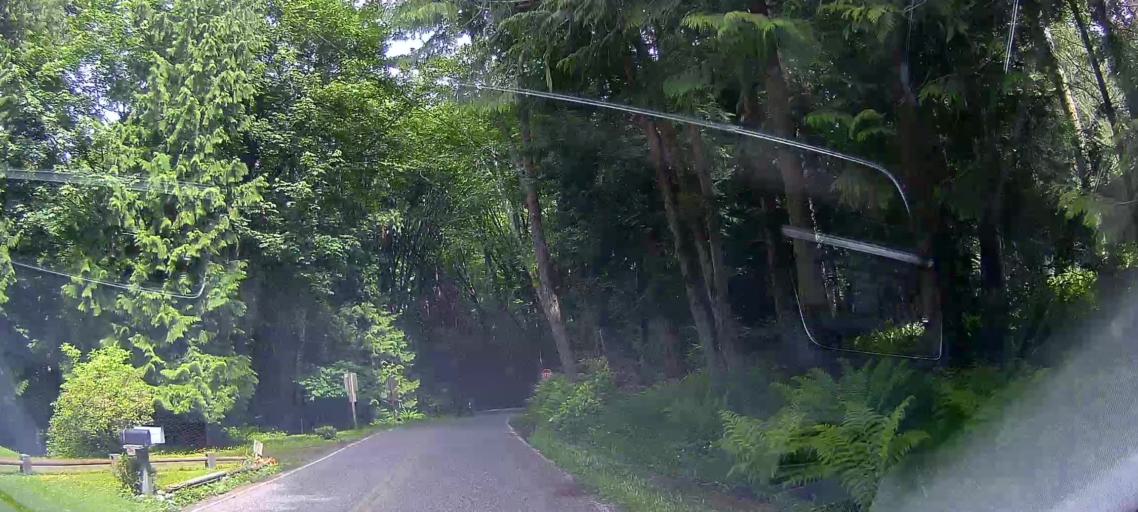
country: US
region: Washington
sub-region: Whatcom County
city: Bellingham
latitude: 48.6620
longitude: -122.4927
